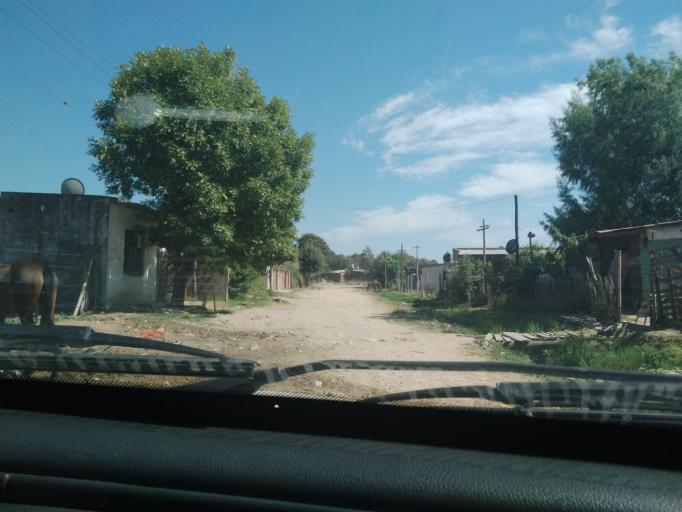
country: AR
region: Corrientes
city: Corrientes
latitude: -27.5112
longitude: -58.8035
